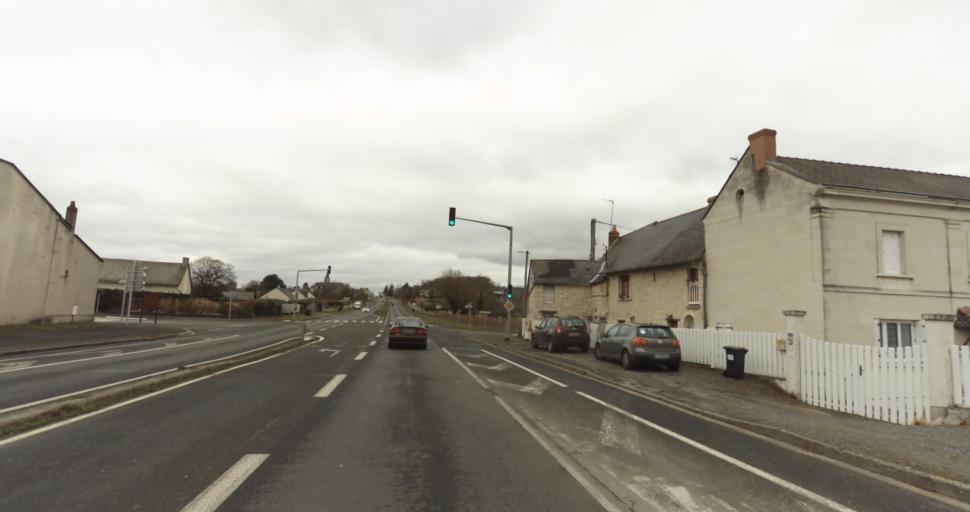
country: FR
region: Pays de la Loire
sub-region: Departement de Maine-et-Loire
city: Varrains
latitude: 47.2227
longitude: -0.0614
